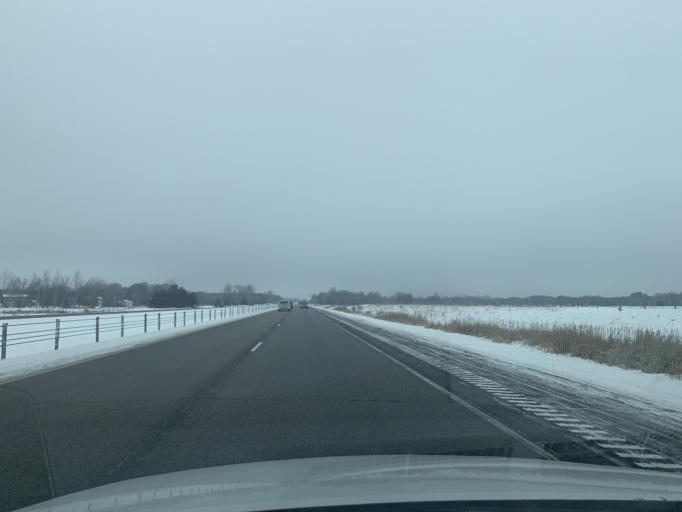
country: US
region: Minnesota
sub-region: Chisago County
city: Branch
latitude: 45.4761
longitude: -92.9964
